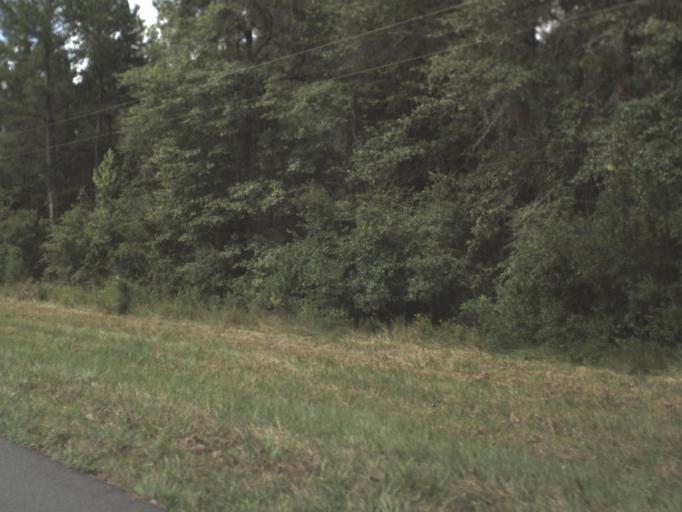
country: US
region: Florida
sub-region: Columbia County
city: Five Points
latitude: 30.4010
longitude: -82.6321
